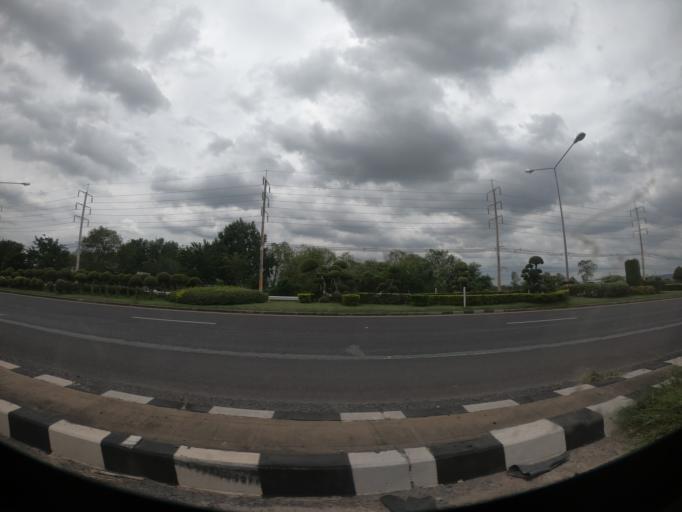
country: TH
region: Nakhon Ratchasima
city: Sikhio
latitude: 14.8693
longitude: 101.7342
